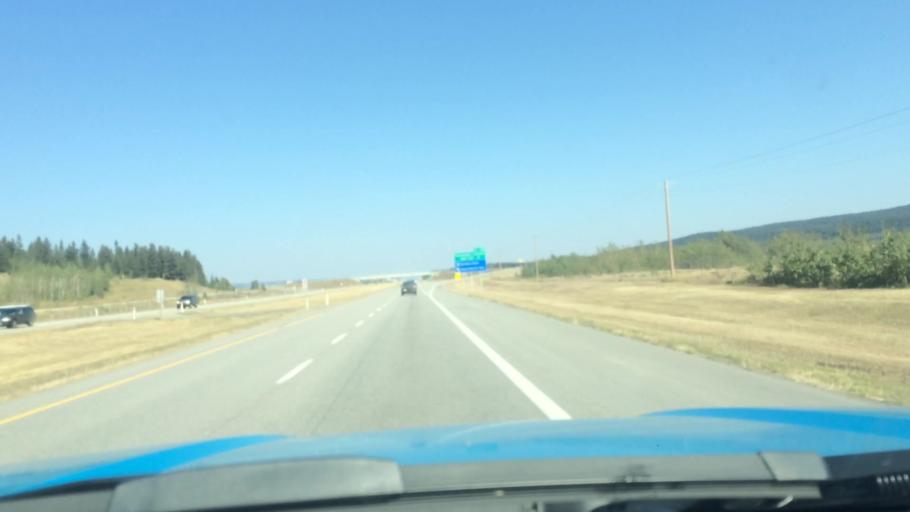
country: CA
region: Alberta
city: Canmore
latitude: 51.0999
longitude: -115.0301
